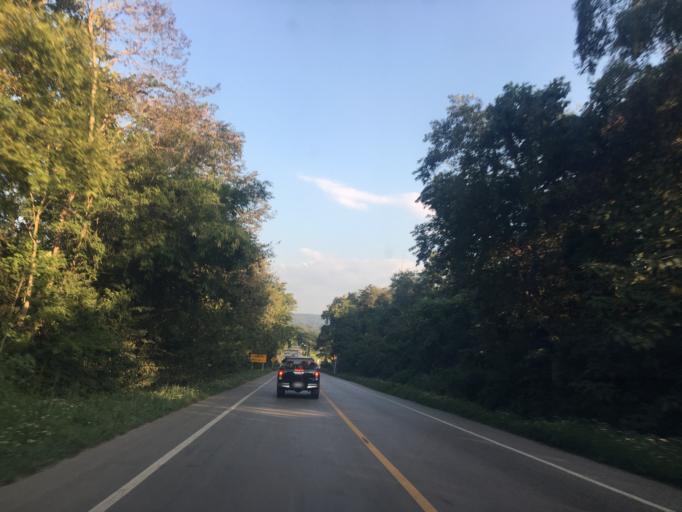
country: TH
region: Lampang
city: Ngao
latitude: 18.6113
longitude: 100.0333
